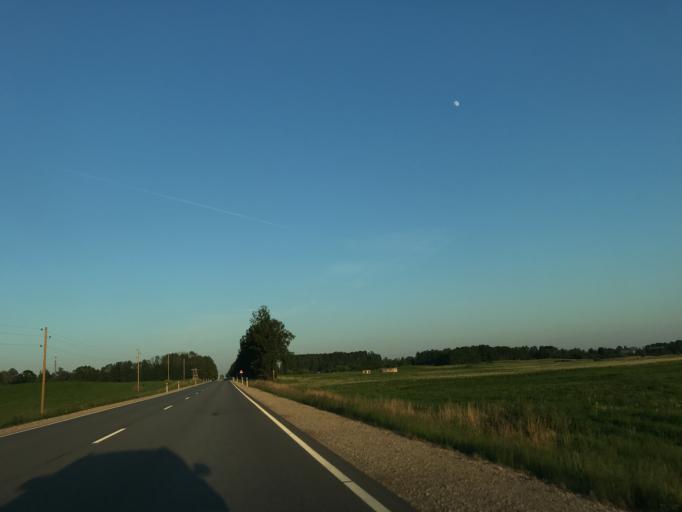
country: LV
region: Vecumnieki
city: Vecumnieki
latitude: 56.5162
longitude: 24.7067
